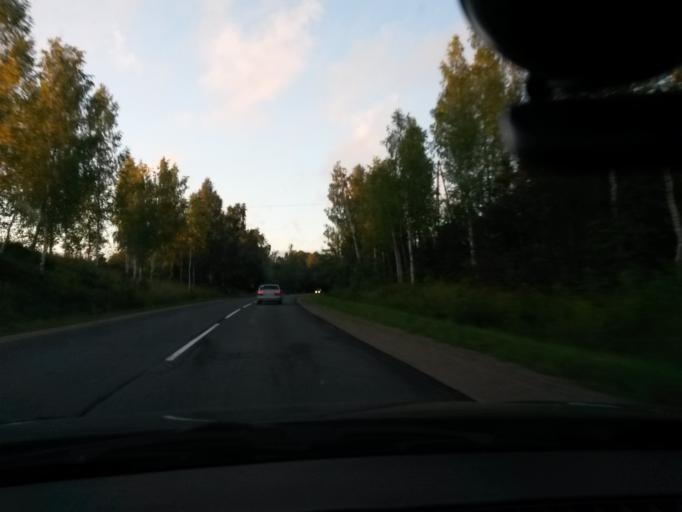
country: LV
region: Madonas Rajons
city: Madona
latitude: 56.7962
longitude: 26.0307
